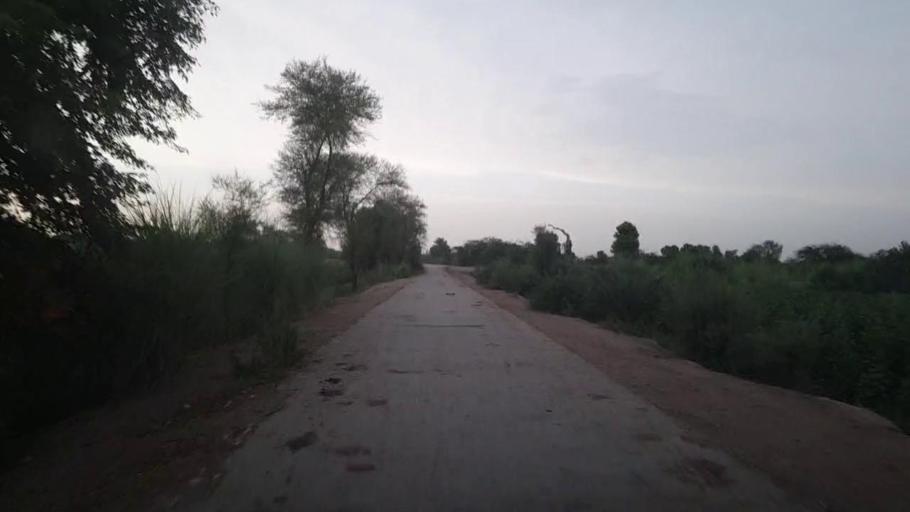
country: PK
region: Sindh
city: Karaundi
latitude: 27.0146
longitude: 68.3539
